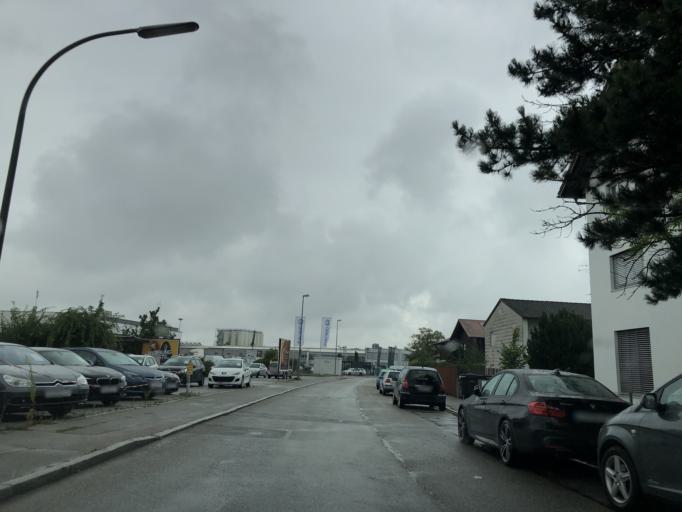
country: DE
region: Bavaria
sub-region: Upper Bavaria
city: Erding
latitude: 48.3120
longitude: 11.8933
